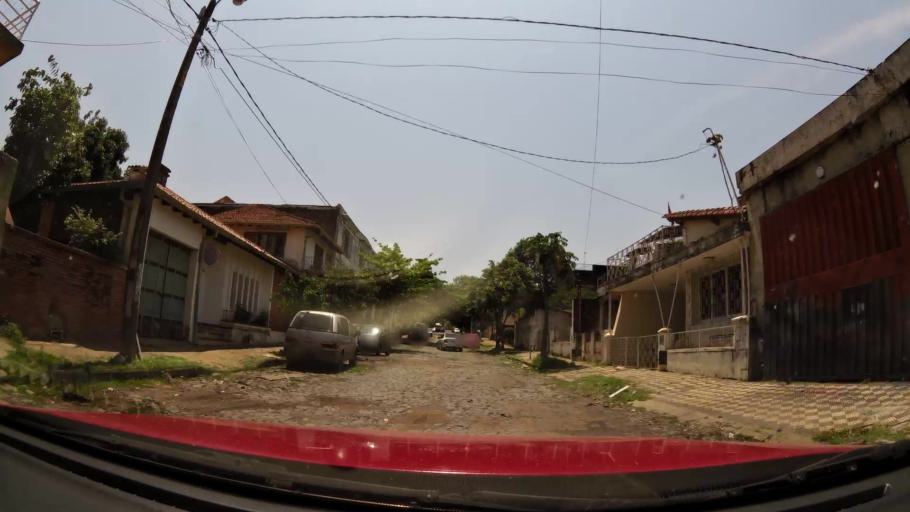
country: PY
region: Asuncion
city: Asuncion
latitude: -25.2946
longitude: -57.6474
